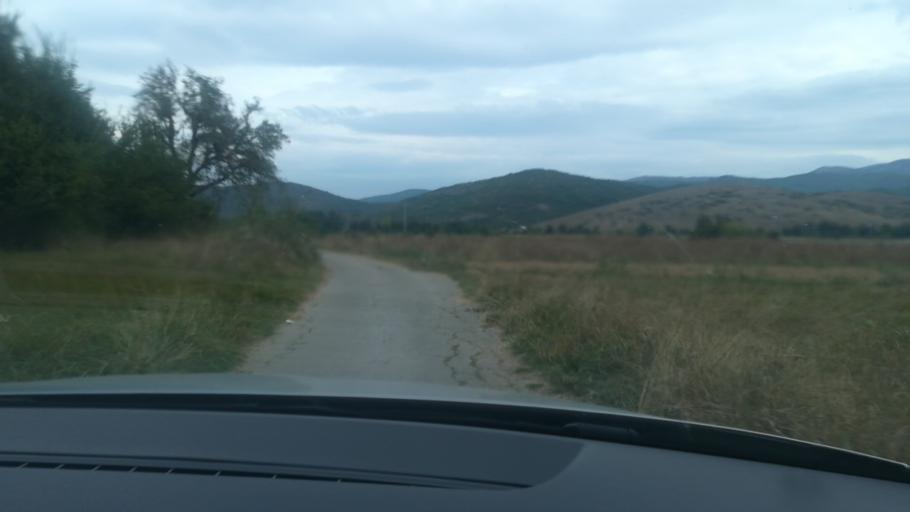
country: MK
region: Debarca
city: Belcista
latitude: 41.2902
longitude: 20.8314
